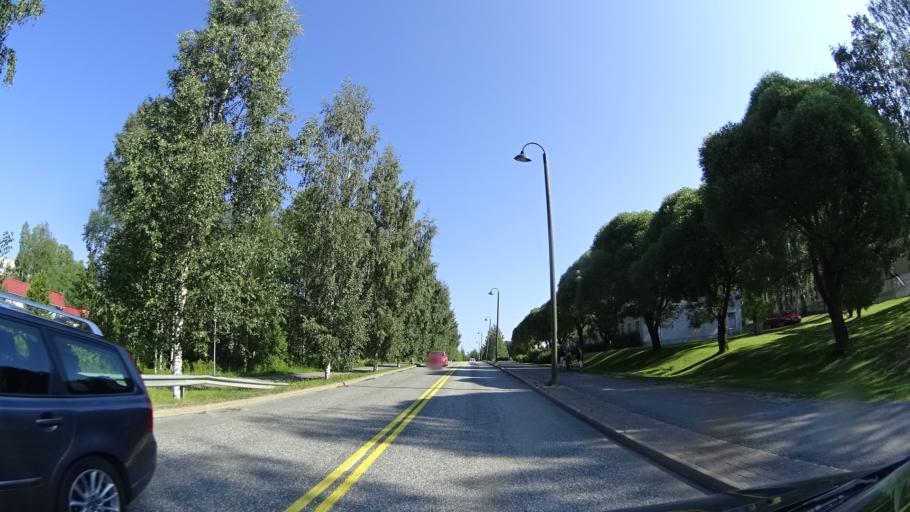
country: FI
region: North Karelia
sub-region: Joensuu
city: Juuka
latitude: 63.2390
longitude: 29.2501
